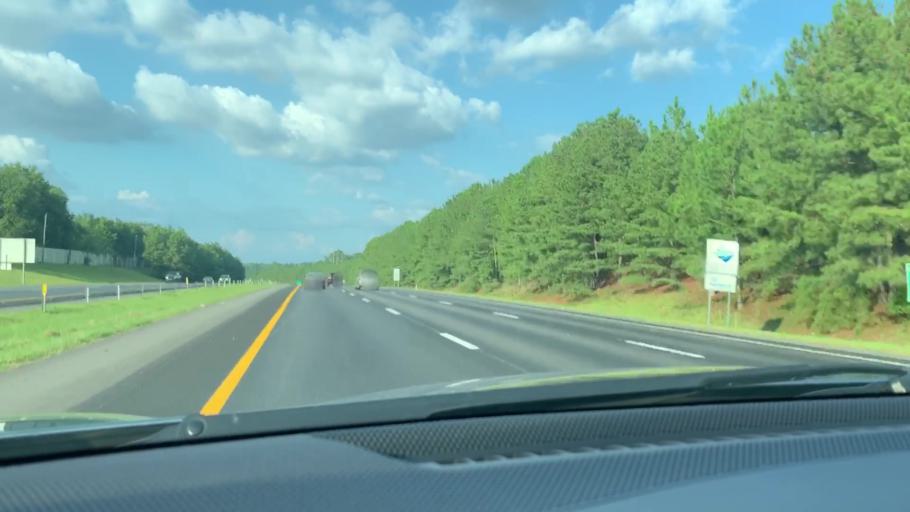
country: US
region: South Carolina
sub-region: Richland County
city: Woodfield
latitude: 34.0301
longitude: -80.9410
